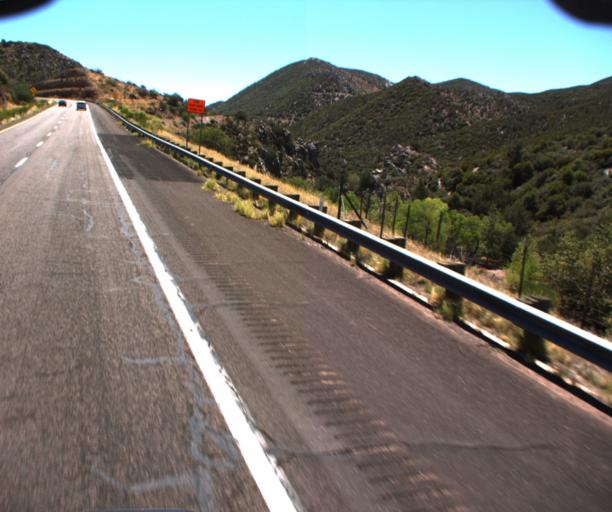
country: US
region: Arizona
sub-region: Gila County
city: Tonto Basin
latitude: 33.9604
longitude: -111.3966
